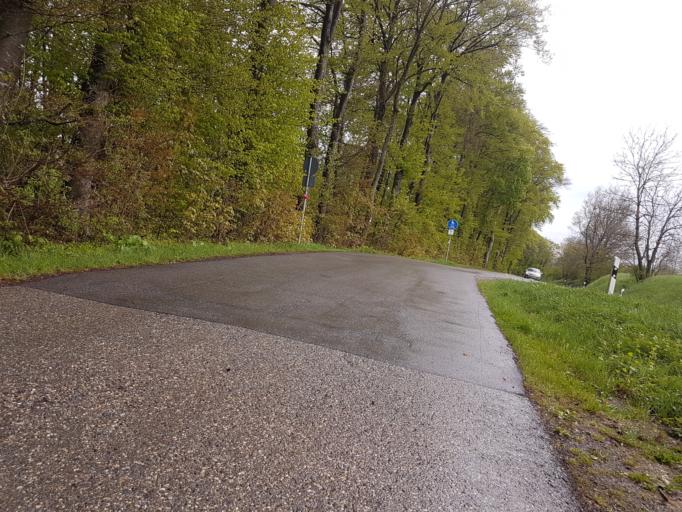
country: DE
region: Baden-Wuerttemberg
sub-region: Freiburg Region
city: Zimmern ob Rottweil
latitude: 48.1772
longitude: 8.6092
